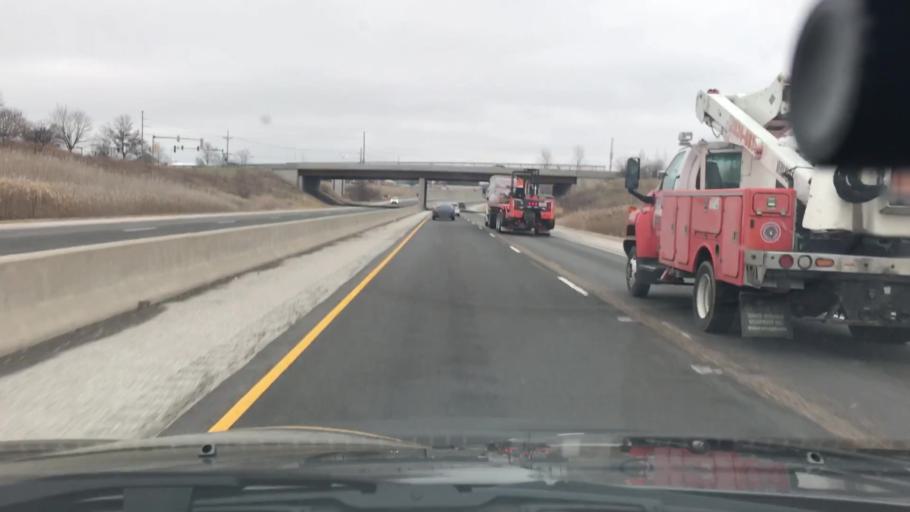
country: US
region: Illinois
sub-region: Madison County
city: Rosewood Heights
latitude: 38.8889
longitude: -90.0608
